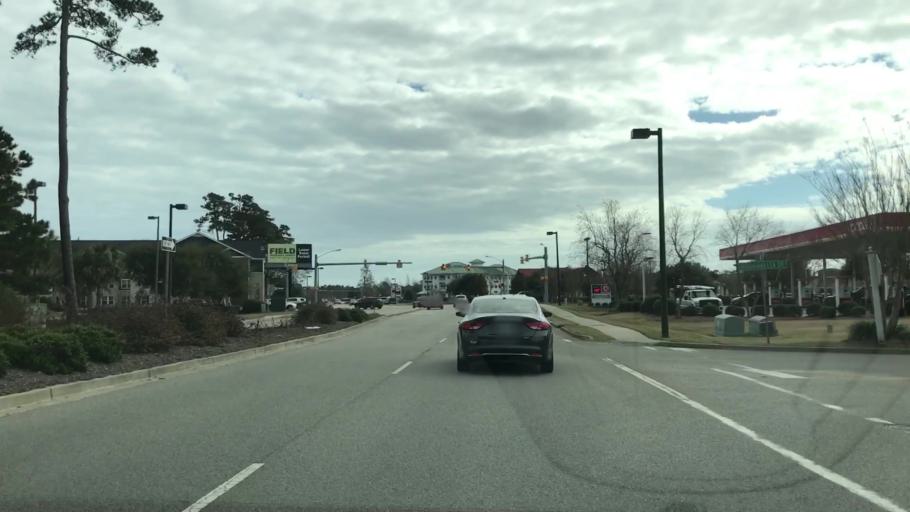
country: US
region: South Carolina
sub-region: Horry County
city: Myrtle Beach
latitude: 33.7275
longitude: -78.8693
